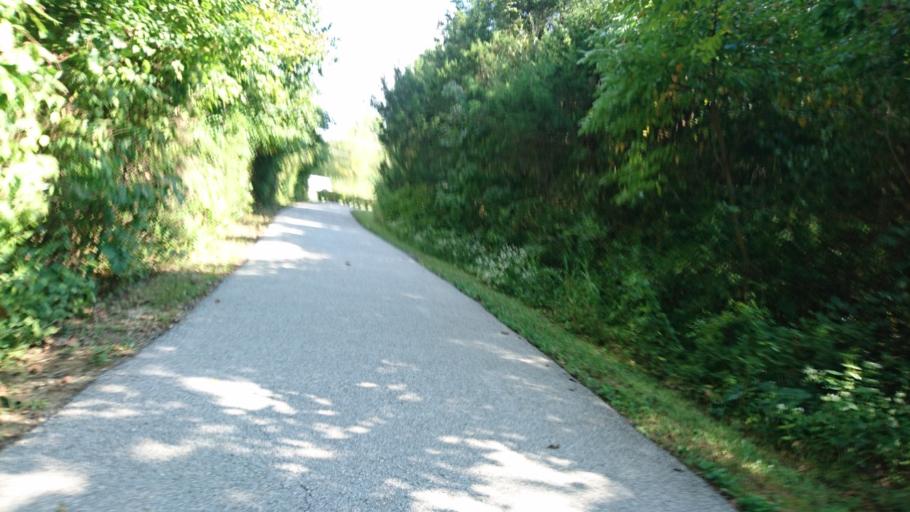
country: US
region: Missouri
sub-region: Saint Louis County
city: Eureka
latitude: 38.5478
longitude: -90.6305
